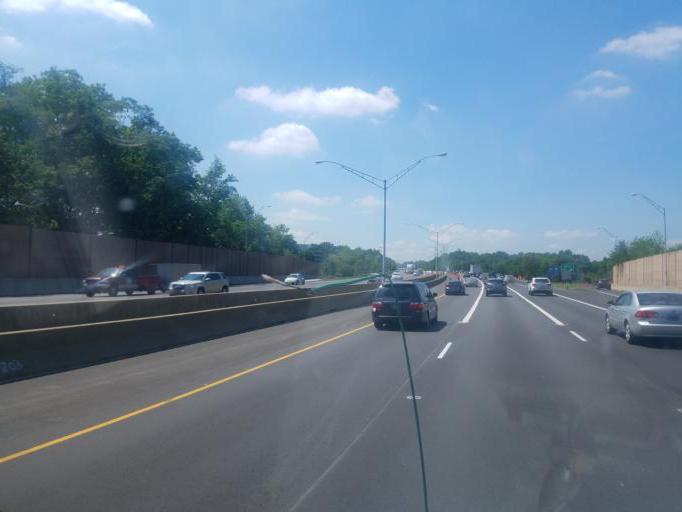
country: US
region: Ohio
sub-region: Hamilton County
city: Blue Ash
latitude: 39.2525
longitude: -84.3650
